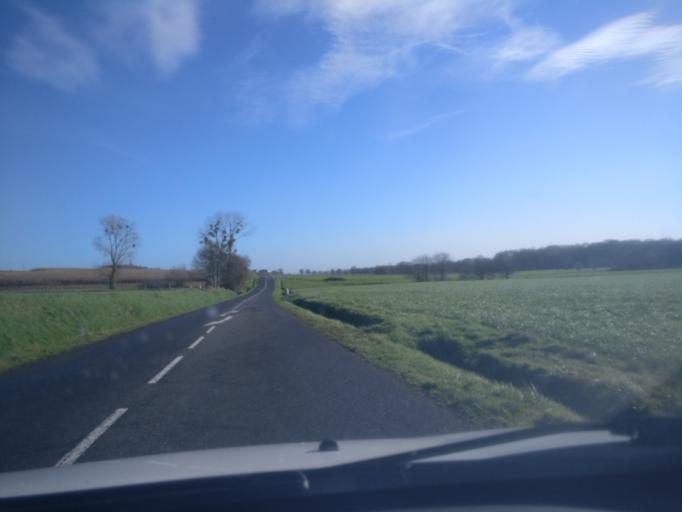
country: FR
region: Brittany
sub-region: Departement d'Ille-et-Vilaine
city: Pleine-Fougeres
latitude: 48.5455
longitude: -1.6000
